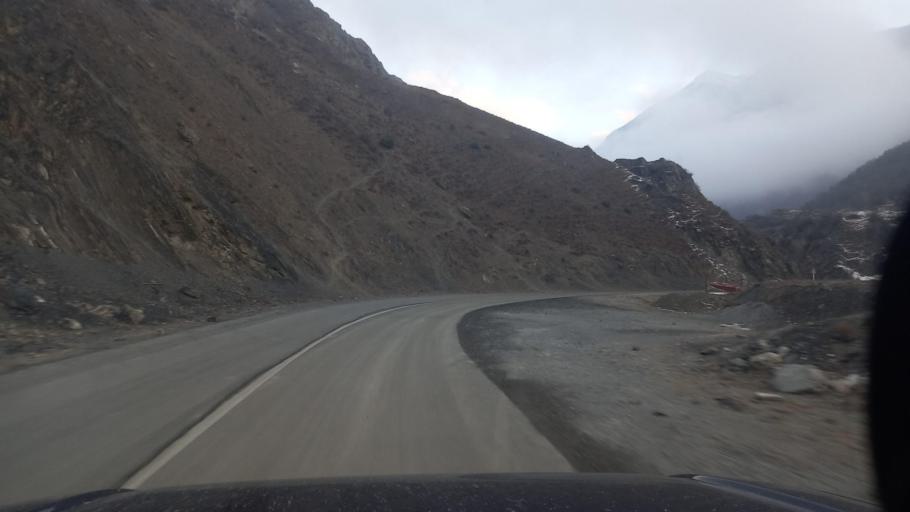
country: RU
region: Ingushetiya
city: Dzhayrakh
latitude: 42.8011
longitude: 44.7580
